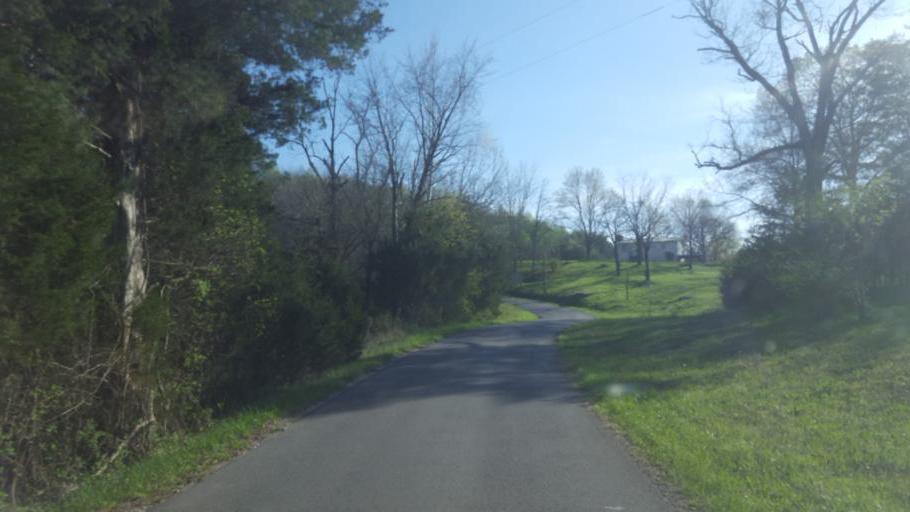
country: US
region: Kentucky
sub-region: Barren County
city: Cave City
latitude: 37.1917
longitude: -86.0140
